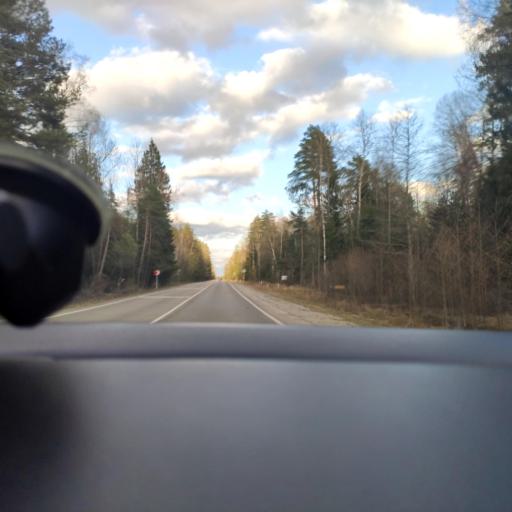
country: RU
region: Moskovskaya
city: Shaturtorf
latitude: 55.4304
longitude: 39.3605
